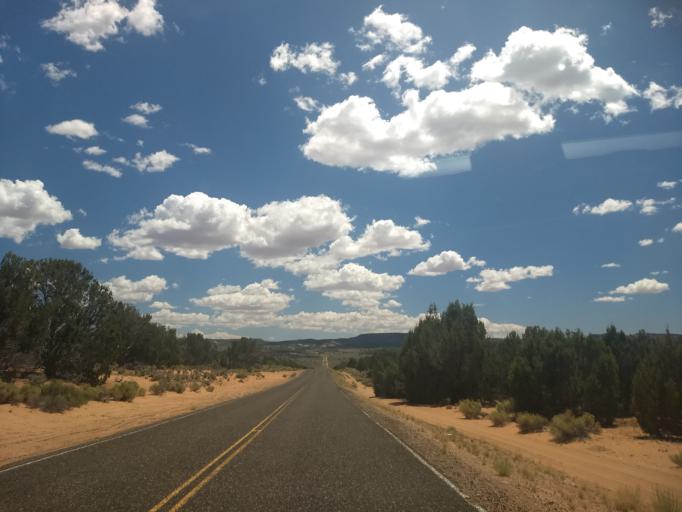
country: US
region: Utah
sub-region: Kane County
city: Kanab
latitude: 37.1752
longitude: -112.6600
